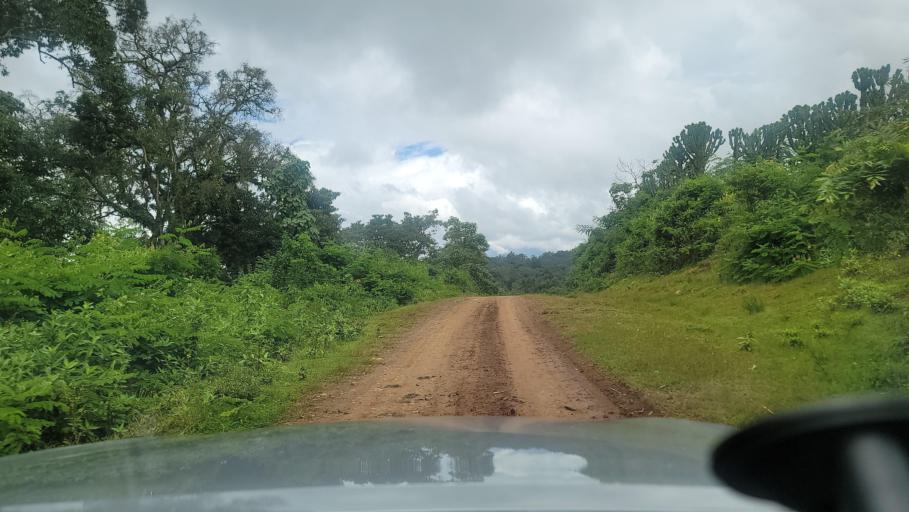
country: ET
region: Southern Nations, Nationalities, and People's Region
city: Bonga
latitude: 7.6345
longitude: 36.2240
